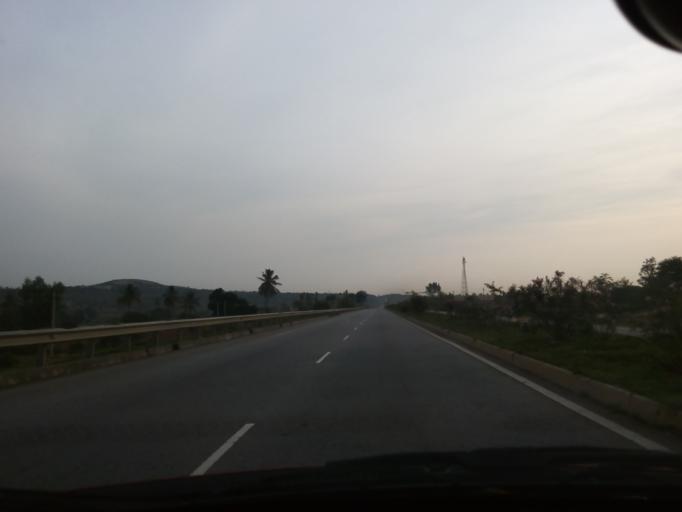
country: IN
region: Karnataka
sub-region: Chikkaballapur
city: Chik Ballapur
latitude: 13.5365
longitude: 77.7678
